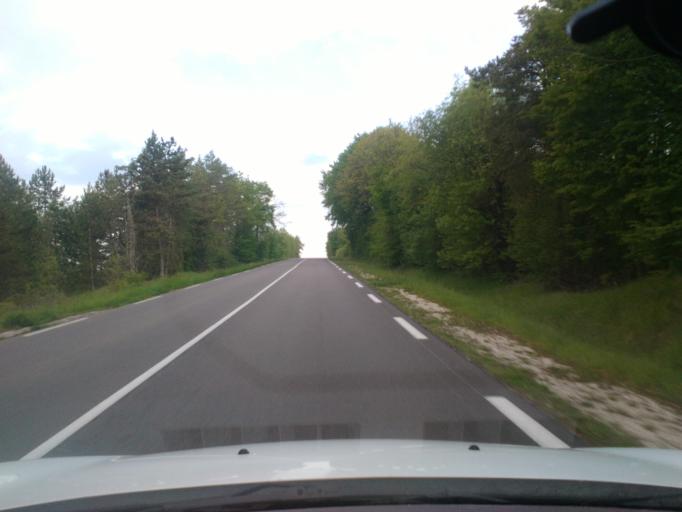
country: FR
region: Champagne-Ardenne
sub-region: Departement de la Haute-Marne
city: Lavilleneuve-au-Roi
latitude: 48.1944
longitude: 4.9516
